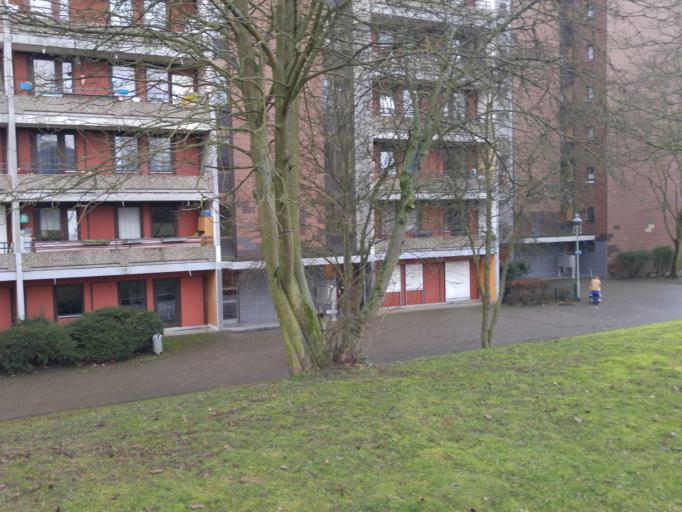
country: DE
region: Hesse
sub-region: Regierungsbezirk Darmstadt
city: Bad Homburg vor der Hoehe
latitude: 50.1881
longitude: 8.6613
